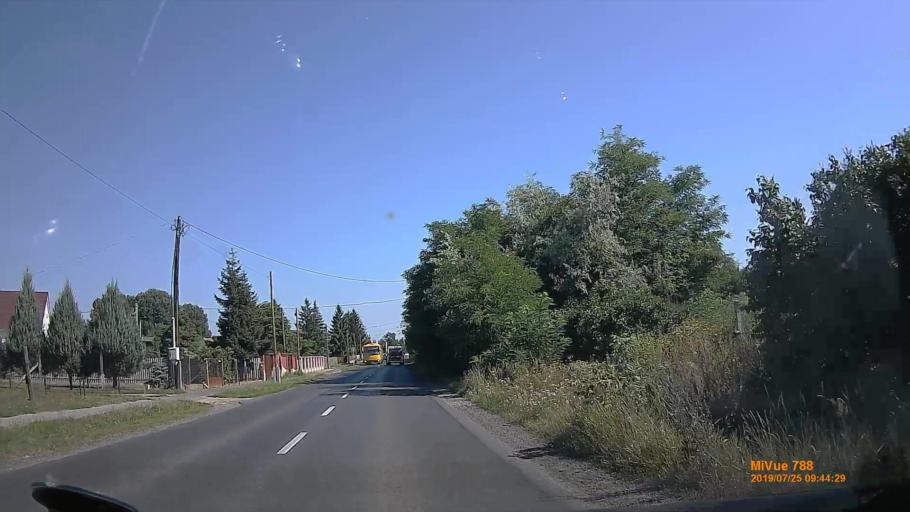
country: HU
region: Szabolcs-Szatmar-Bereg
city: Kotaj
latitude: 48.0267
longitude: 21.7453
